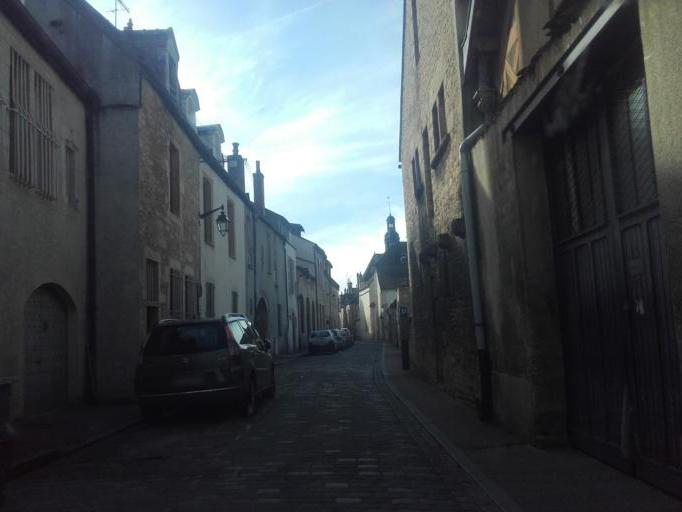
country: FR
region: Bourgogne
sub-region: Departement de la Cote-d'Or
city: Beaune
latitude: 47.0244
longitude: 4.8406
